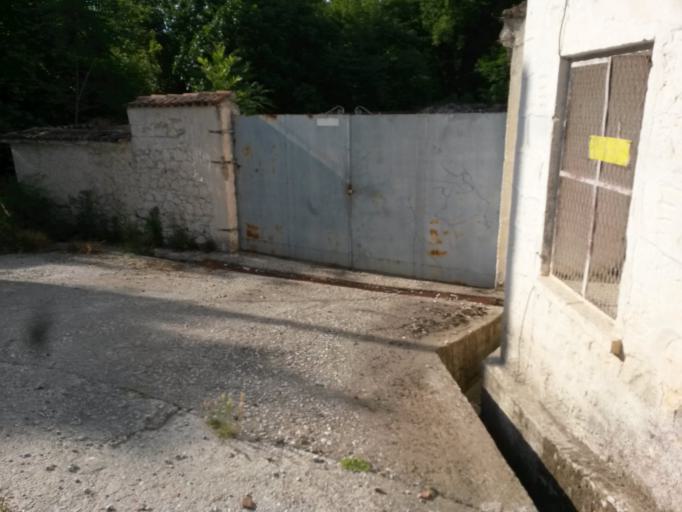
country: GR
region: North Aegean
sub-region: Nomos Lesvou
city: Agiasos
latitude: 39.1094
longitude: 26.3943
